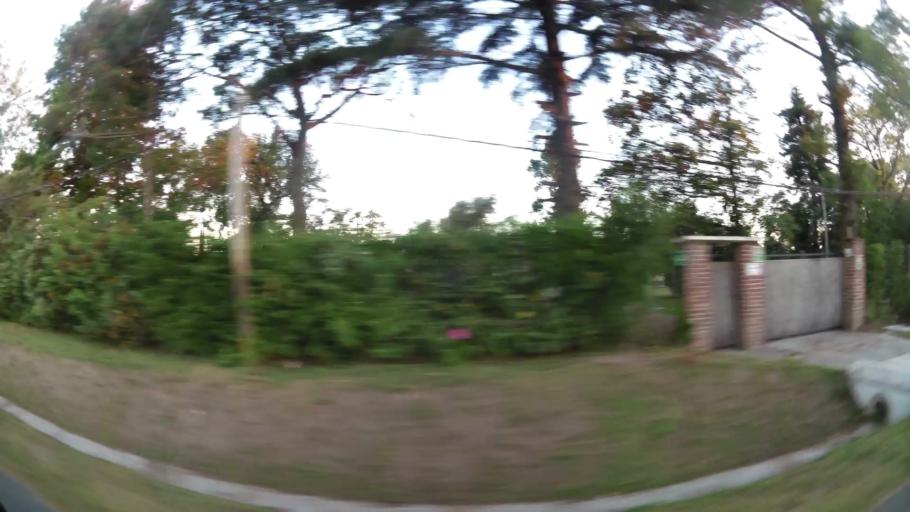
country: UY
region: Canelones
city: Barra de Carrasco
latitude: -34.8359
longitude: -55.9638
